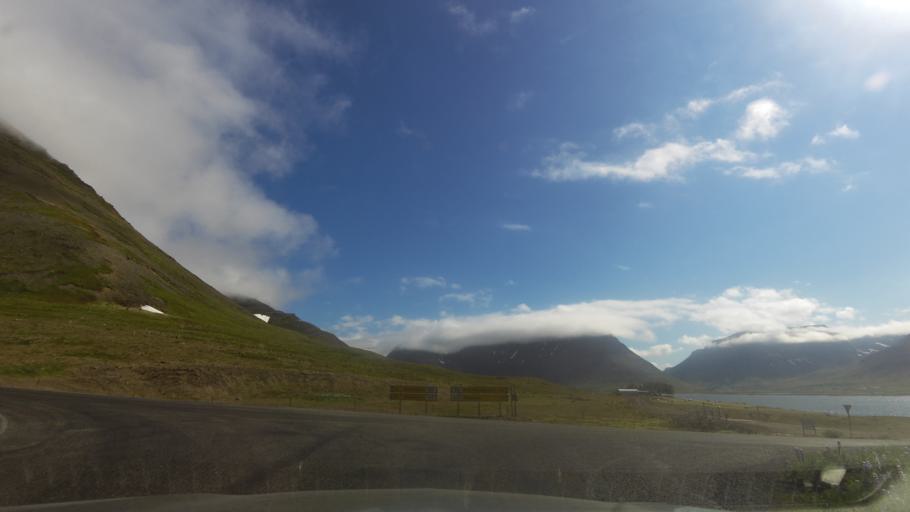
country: IS
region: Westfjords
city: Isafjoerdur
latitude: 66.0161
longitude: -23.4036
